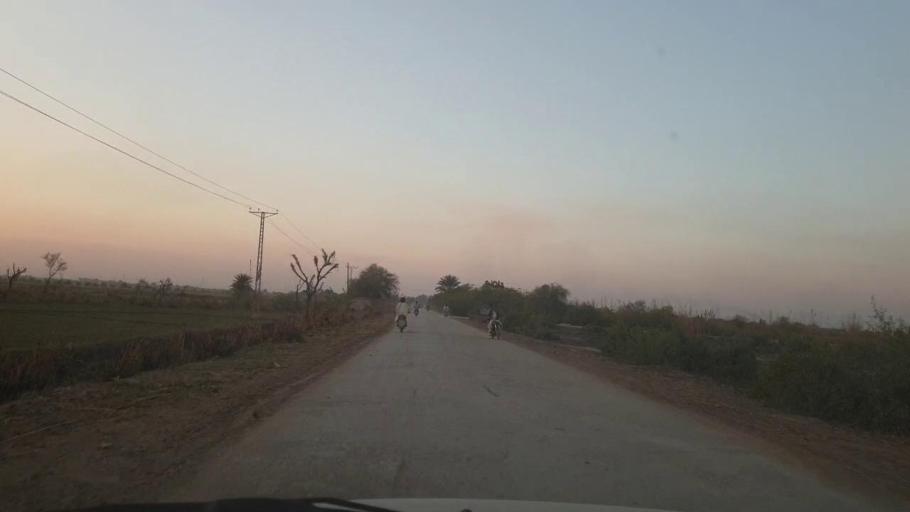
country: PK
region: Sindh
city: Mirpur Khas
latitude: 25.4965
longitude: 69.0368
